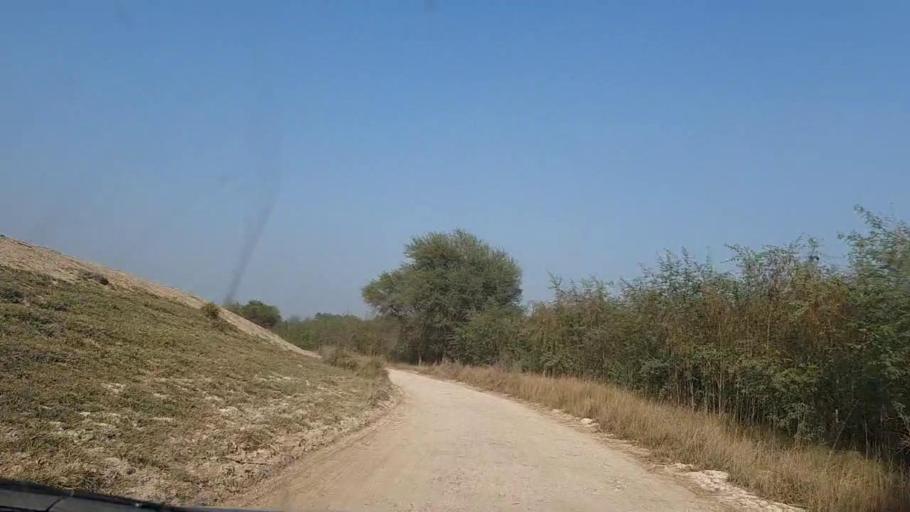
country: PK
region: Sindh
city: Moro
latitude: 26.8111
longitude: 67.9550
